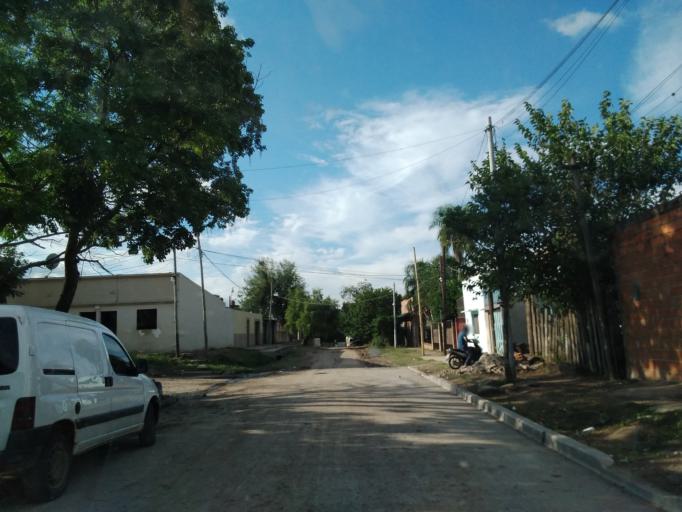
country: AR
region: Corrientes
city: Corrientes
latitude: -27.4597
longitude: -58.8163
